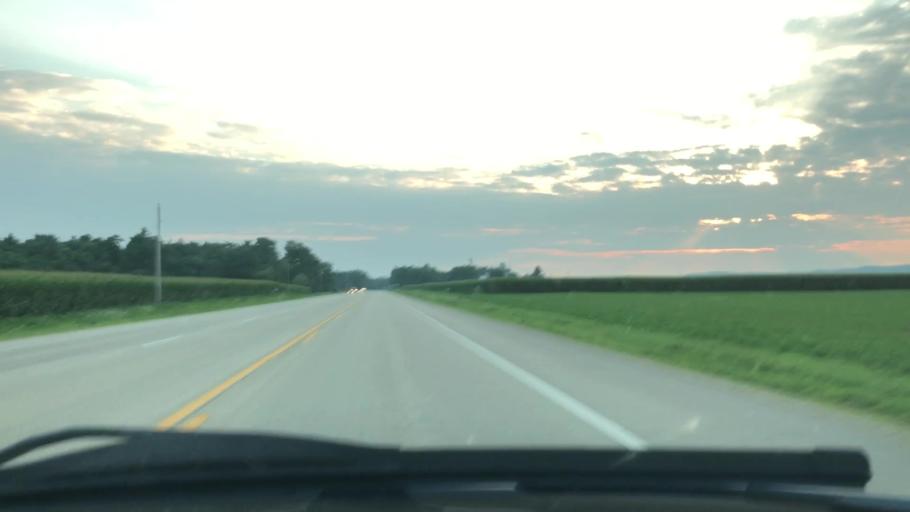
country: US
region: Wisconsin
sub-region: Sauk County
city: Spring Green
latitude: 43.1897
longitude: -90.1269
